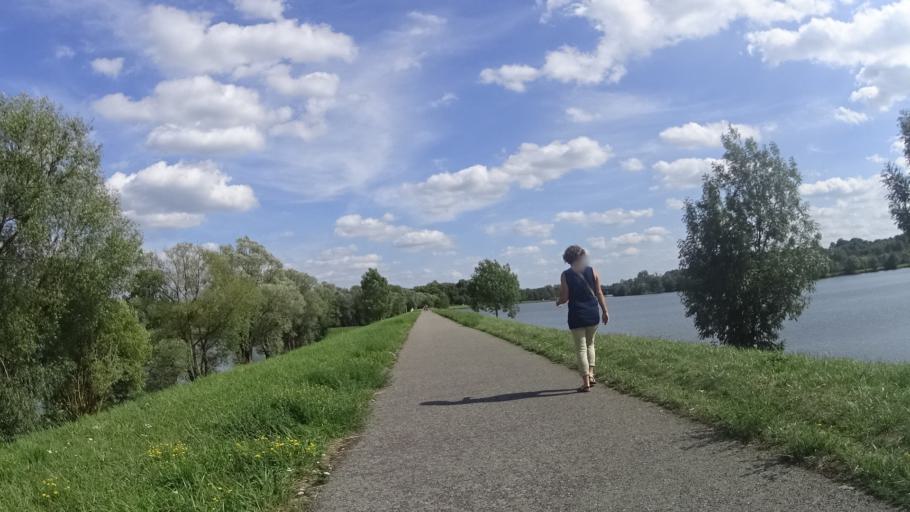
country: FR
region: Lorraine
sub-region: Departement de Meurthe-et-Moselle
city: Dommartin-les-Toul
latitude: 48.6632
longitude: 5.8934
